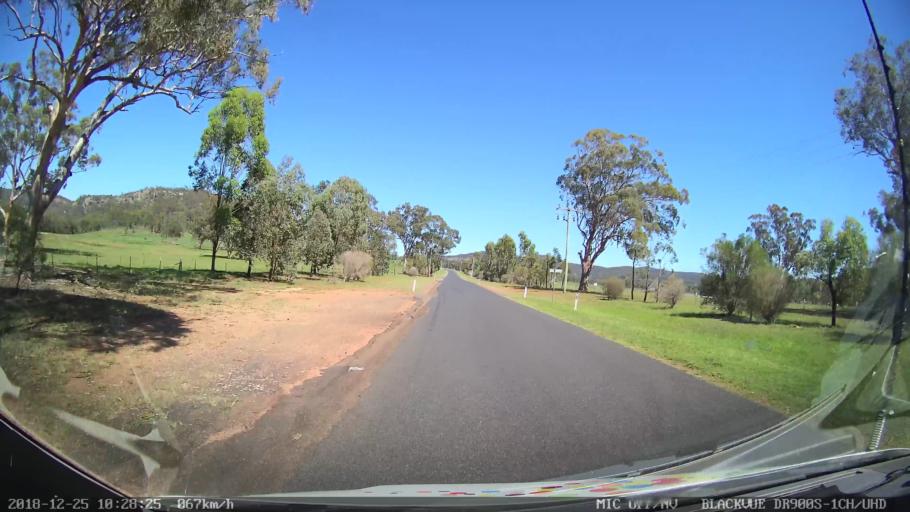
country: AU
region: New South Wales
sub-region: Muswellbrook
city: Denman
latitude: -32.3820
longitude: 150.4642
